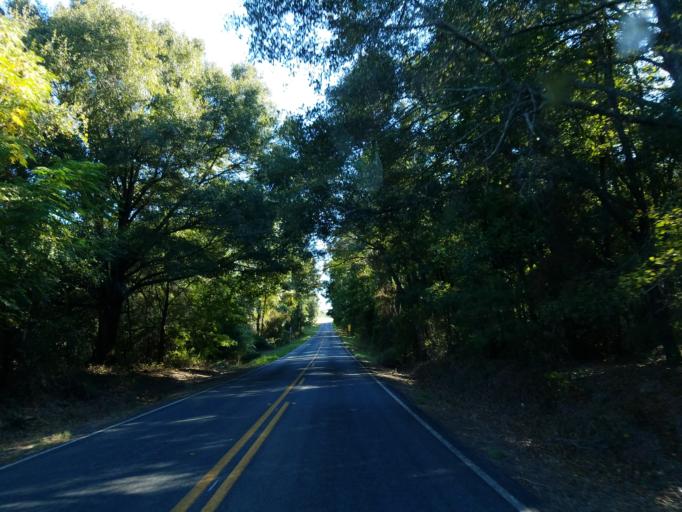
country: US
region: Georgia
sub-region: Dooly County
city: Unadilla
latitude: 32.2266
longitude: -83.8826
